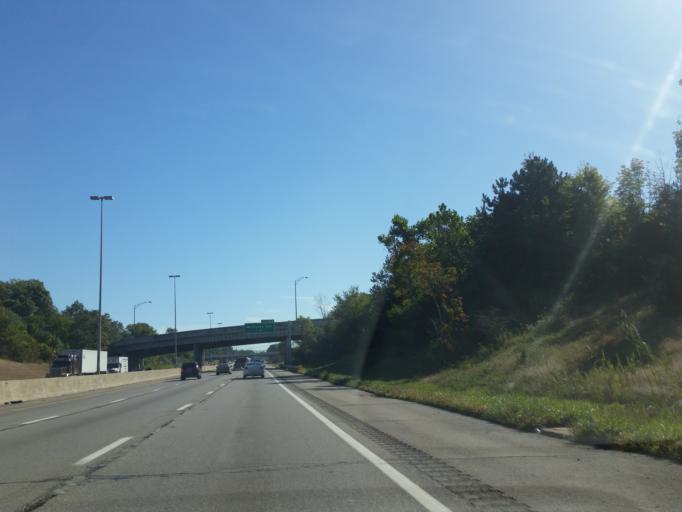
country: US
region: Ohio
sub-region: Cuyahoga County
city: Rocky River
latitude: 41.4719
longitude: -81.8424
